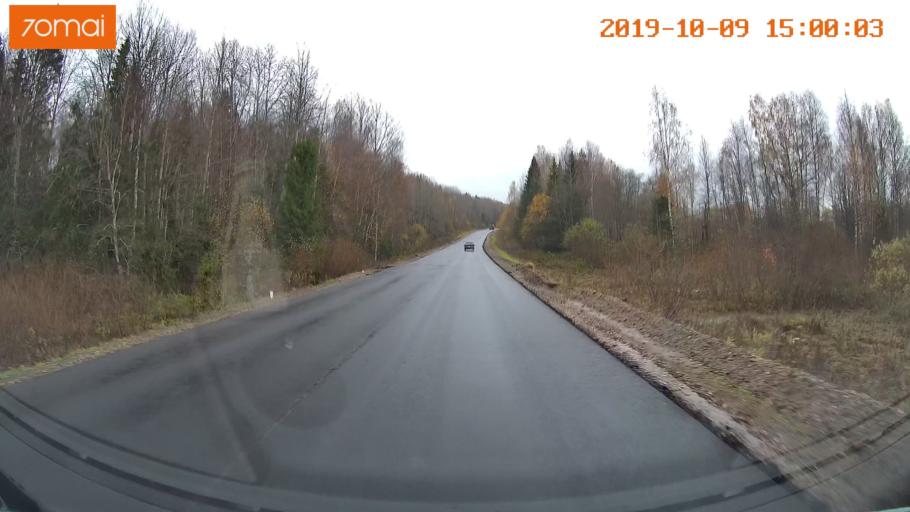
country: RU
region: Kostroma
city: Chistyye Bory
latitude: 58.3135
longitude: 41.6751
